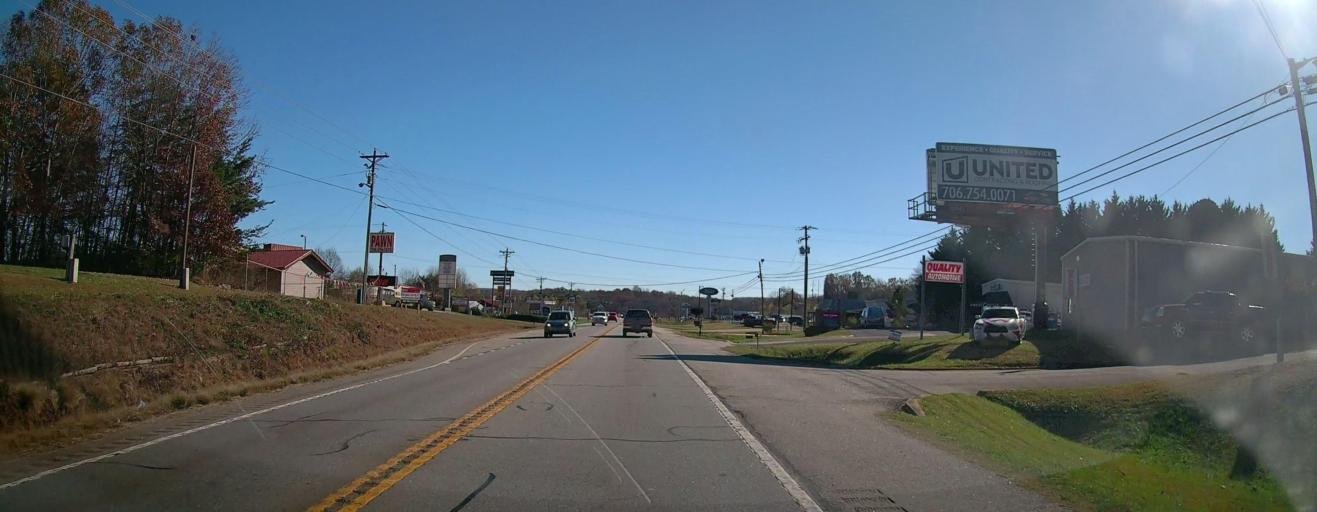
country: US
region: Georgia
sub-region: White County
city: Cleveland
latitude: 34.5607
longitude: -83.7628
